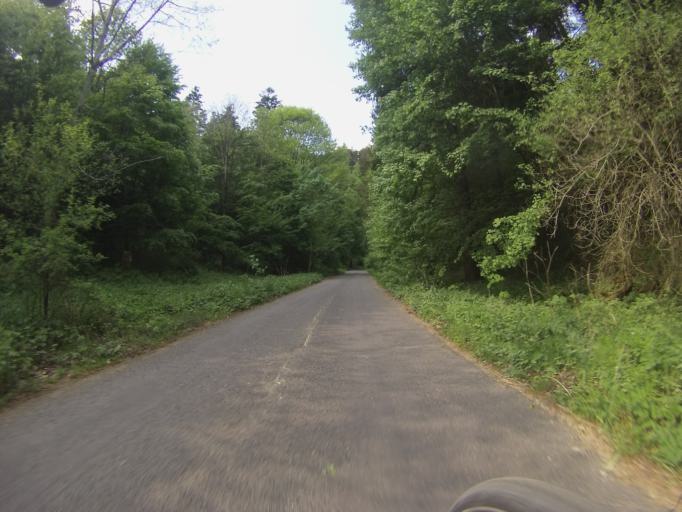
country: CZ
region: South Moravian
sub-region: Okres Blansko
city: Jedovnice
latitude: 49.3662
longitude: 16.7282
